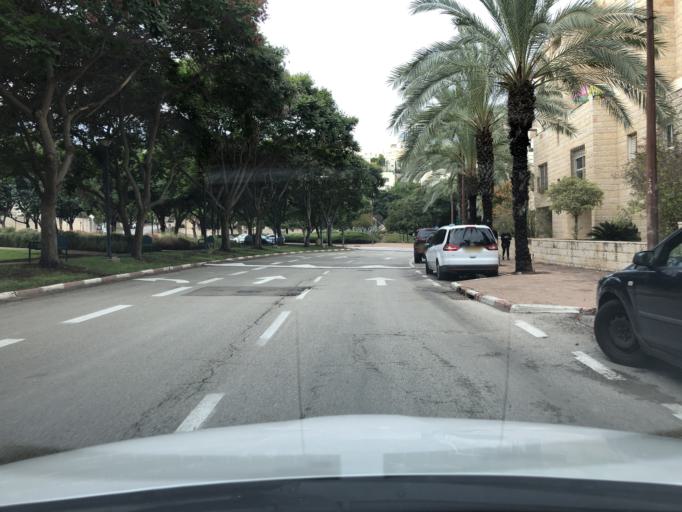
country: IL
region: Central District
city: Modiin
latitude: 31.8961
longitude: 35.0136
